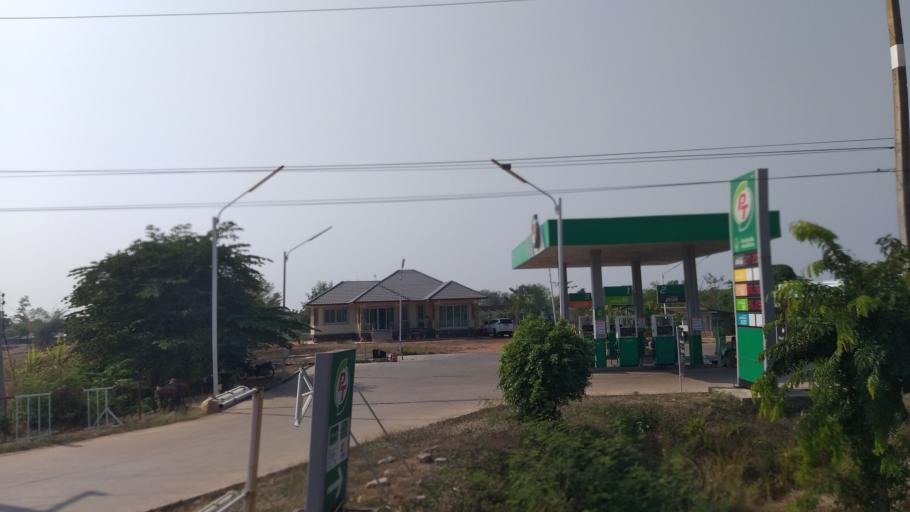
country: TH
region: Changwat Udon Thani
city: Thung Fon
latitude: 17.5489
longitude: 103.2357
